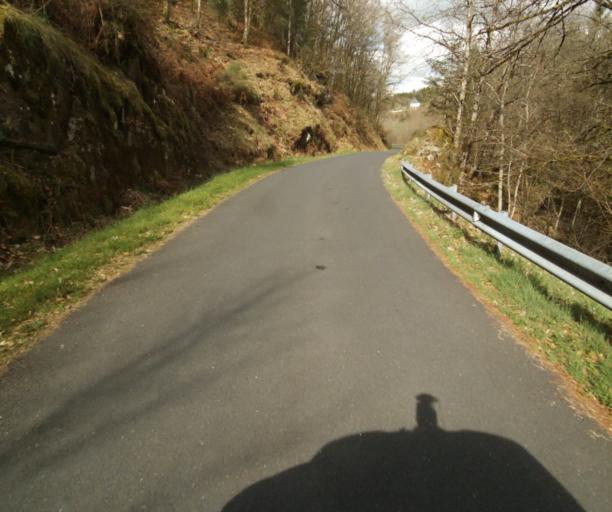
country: FR
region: Limousin
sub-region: Departement de la Correze
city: Correze
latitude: 45.3715
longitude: 1.8850
